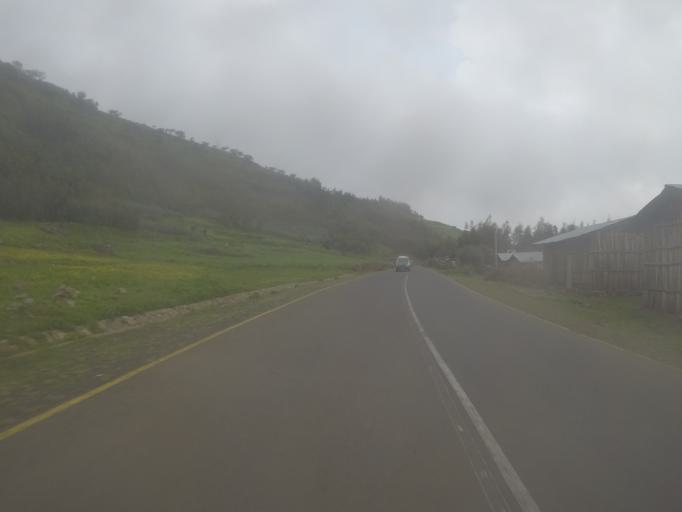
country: ET
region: Amhara
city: Gondar
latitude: 12.7271
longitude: 37.5113
